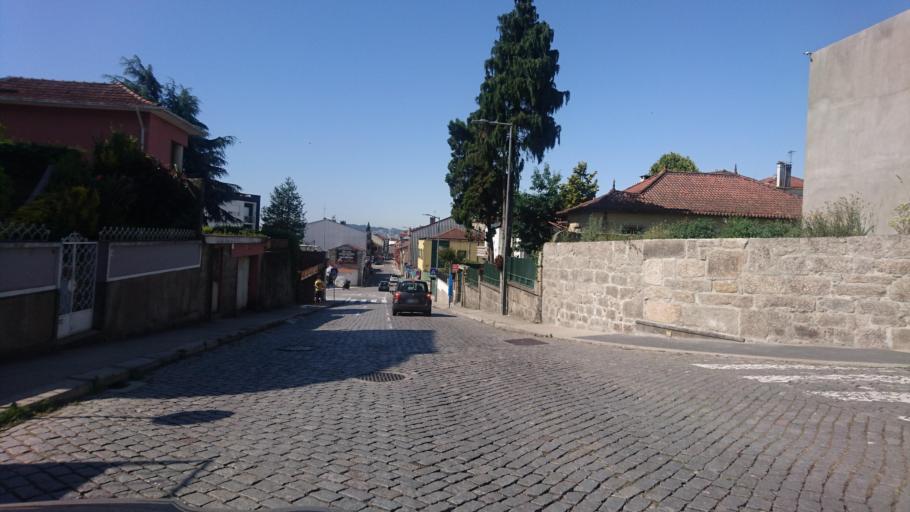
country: PT
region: Porto
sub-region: Gondomar
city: Rio Tinto
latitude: 41.1666
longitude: -8.5706
